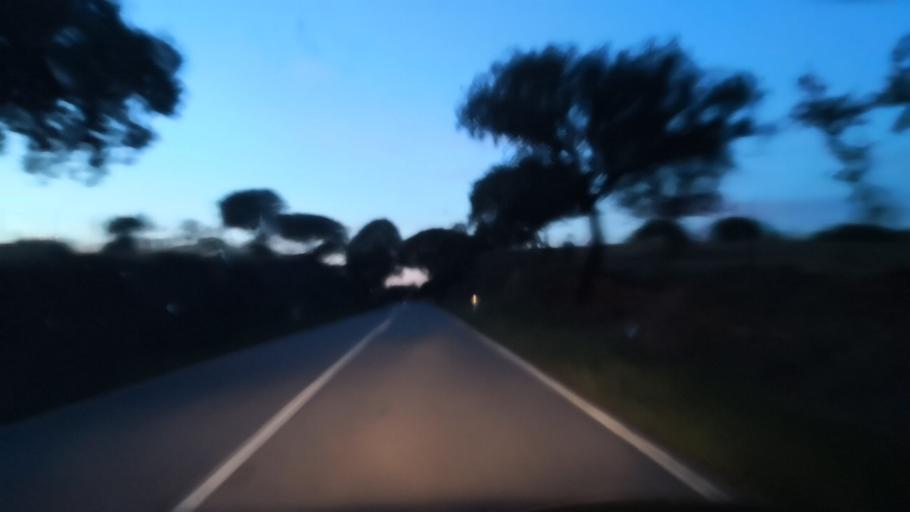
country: ES
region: Extremadura
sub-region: Provincia de Caceres
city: Piedras Albas
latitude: 39.8481
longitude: -6.9818
